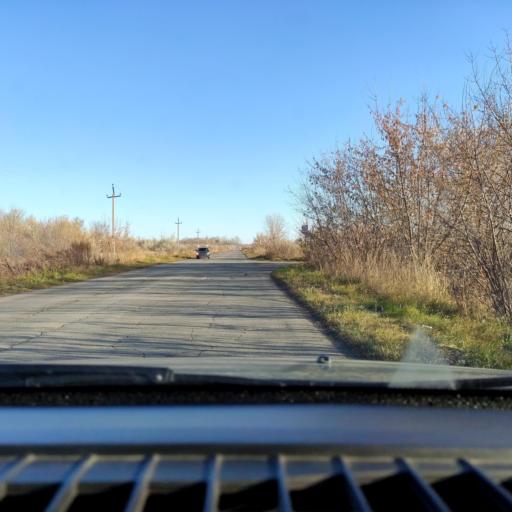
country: RU
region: Samara
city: Tol'yatti
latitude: 53.6340
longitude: 49.3061
